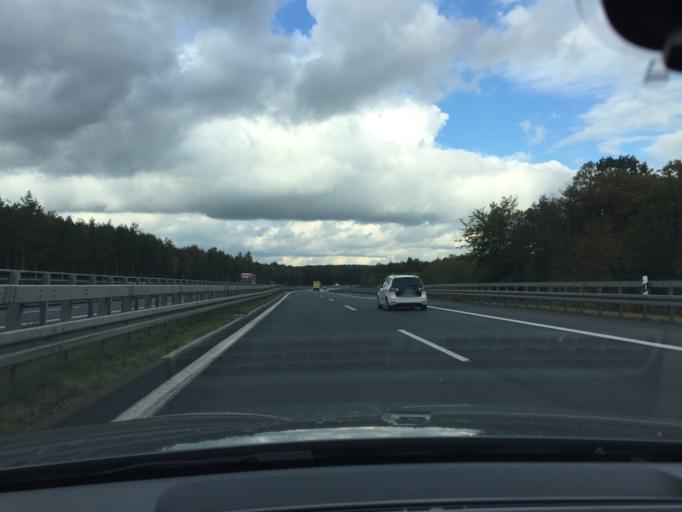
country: DE
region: Brandenburg
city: Grosskmehlen
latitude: 51.3414
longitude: 13.7175
